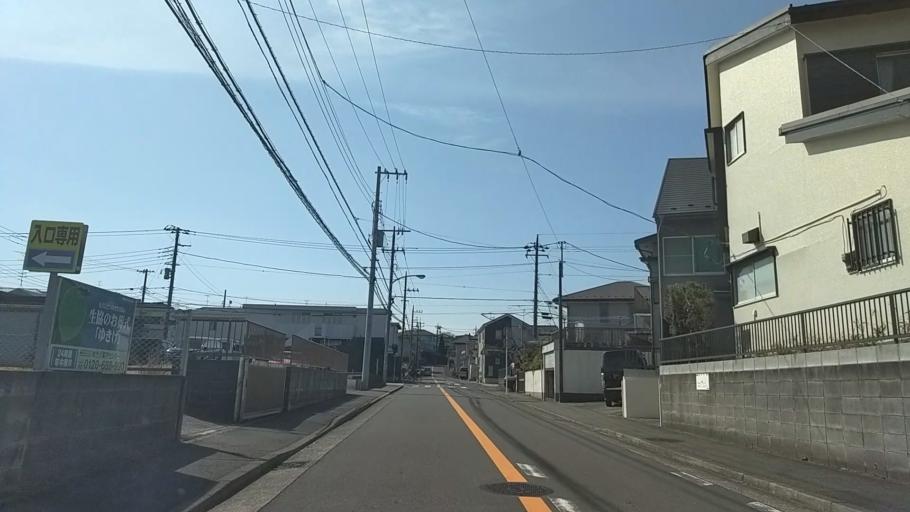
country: JP
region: Kanagawa
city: Kamakura
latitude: 35.3917
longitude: 139.5557
